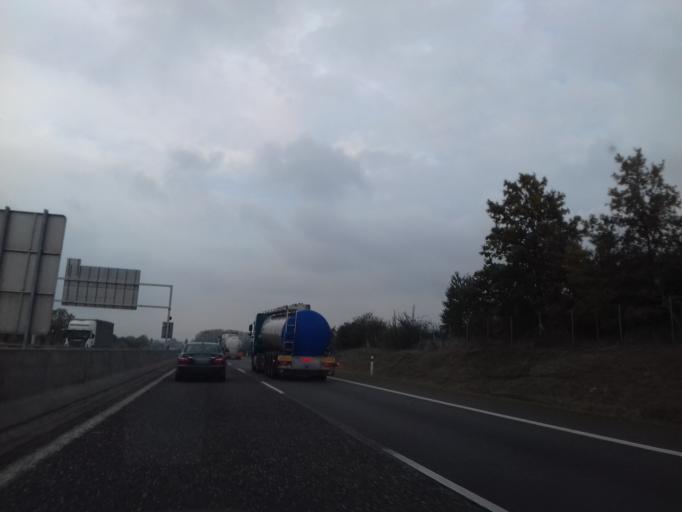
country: SK
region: Bratislavsky
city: Stupava
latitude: 48.2152
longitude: 17.0338
